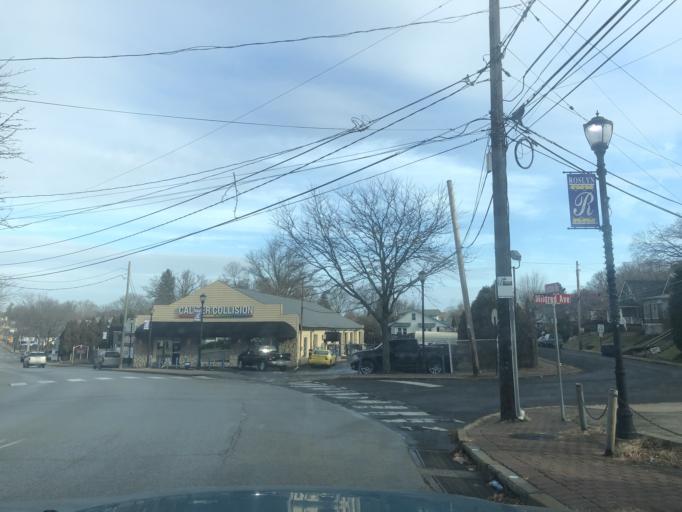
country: US
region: Pennsylvania
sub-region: Montgomery County
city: Jenkintown
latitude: 40.1223
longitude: -75.1327
